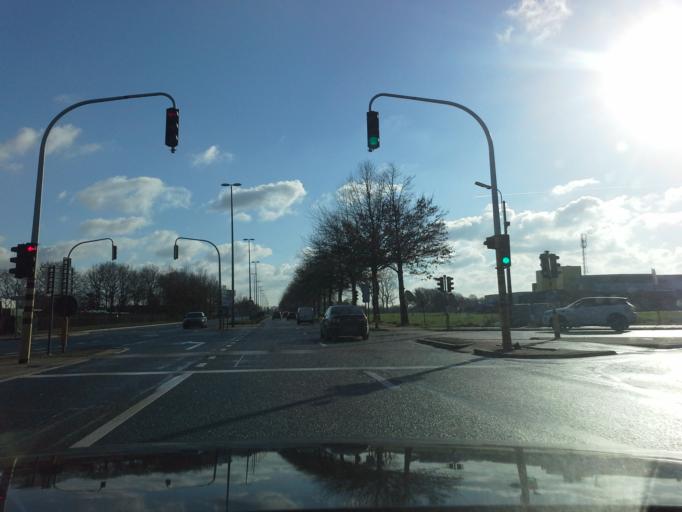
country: BE
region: Flanders
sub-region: Provincie Antwerpen
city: Geel
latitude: 51.1594
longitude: 4.9683
